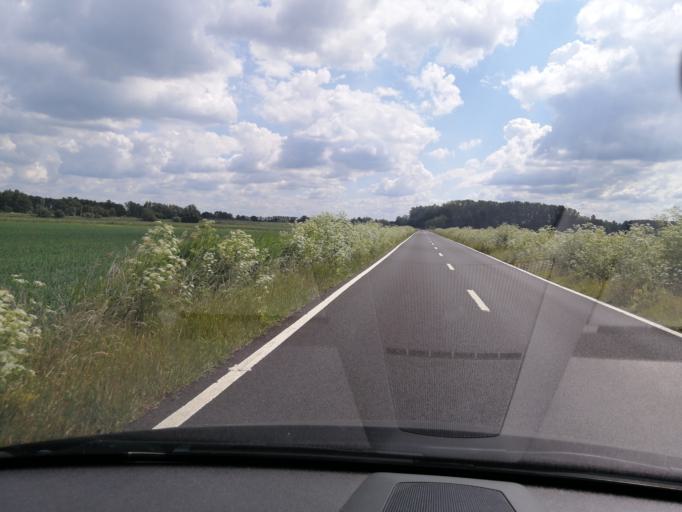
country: GB
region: England
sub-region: Cambridgeshire
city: Yaxley
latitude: 52.4864
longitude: -0.2431
